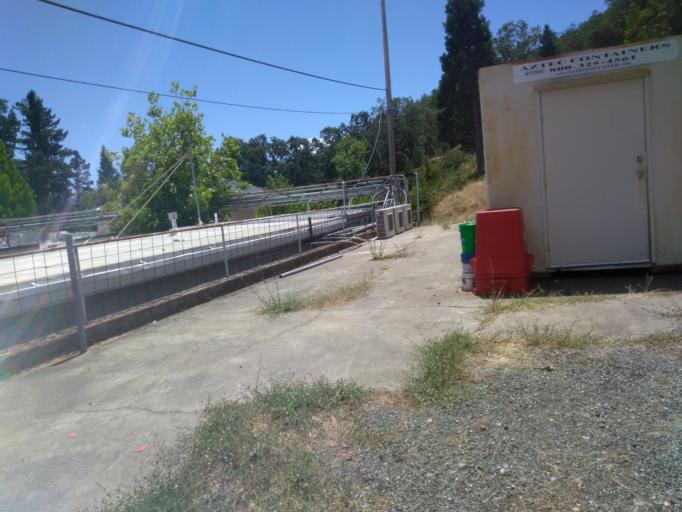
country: US
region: California
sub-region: Mendocino County
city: Ukiah
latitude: 39.1278
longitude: -123.2125
